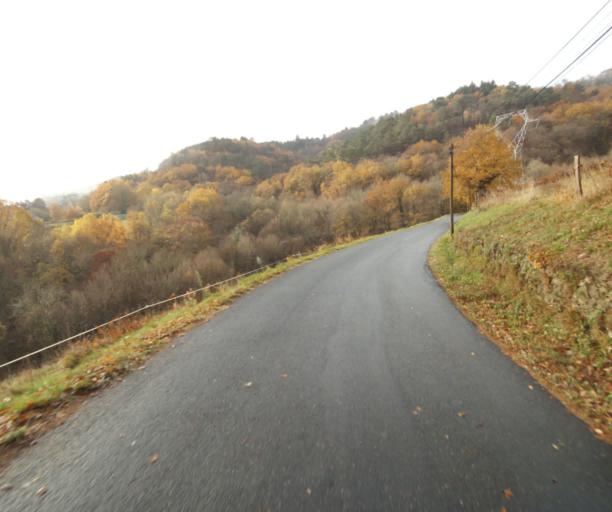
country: FR
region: Limousin
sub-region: Departement de la Correze
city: Cornil
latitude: 45.2017
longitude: 1.6514
